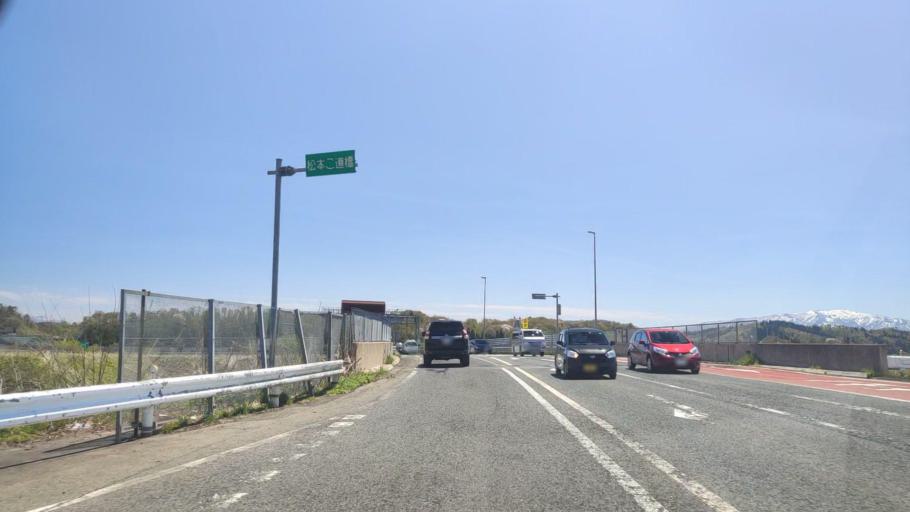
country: JP
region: Yamagata
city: Shinjo
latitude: 38.7413
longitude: 140.2951
